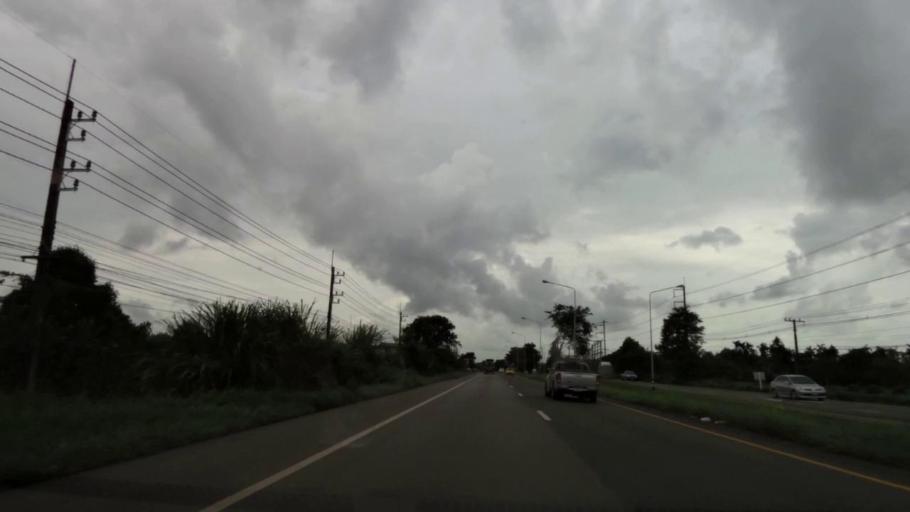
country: TH
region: Chanthaburi
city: Tha Mai
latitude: 12.6923
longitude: 101.9942
